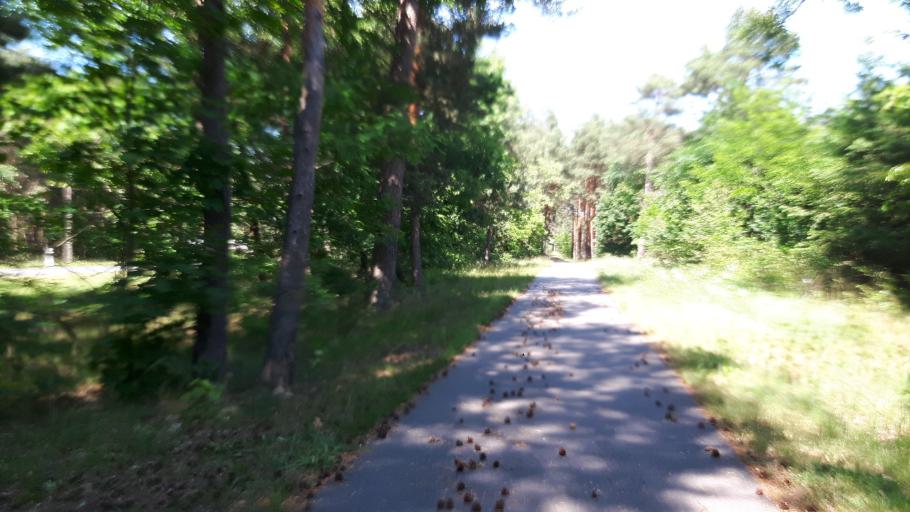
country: DE
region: Brandenburg
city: Treuenbrietzen
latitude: 52.0631
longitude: 12.8272
